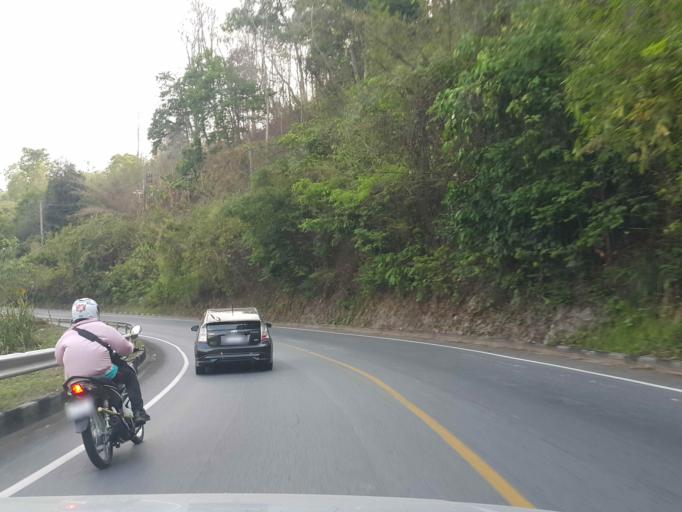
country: TH
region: Chiang Mai
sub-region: Amphoe Chiang Dao
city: Chiang Dao
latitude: 19.2493
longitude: 98.9674
